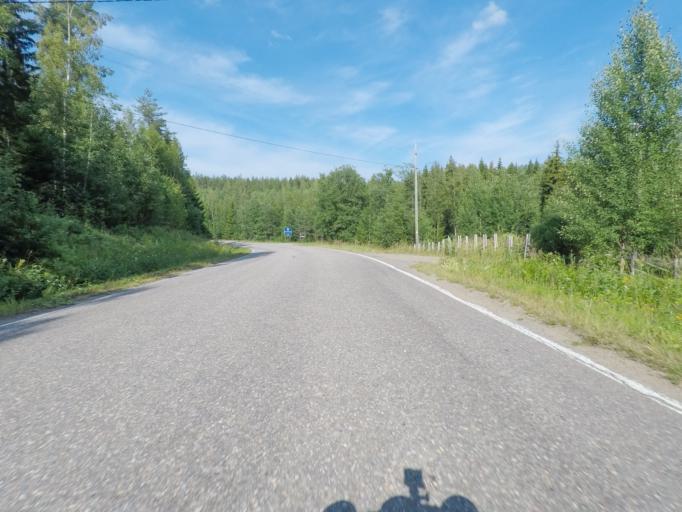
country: FI
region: Southern Savonia
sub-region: Mikkeli
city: Puumala
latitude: 61.6708
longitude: 28.2302
